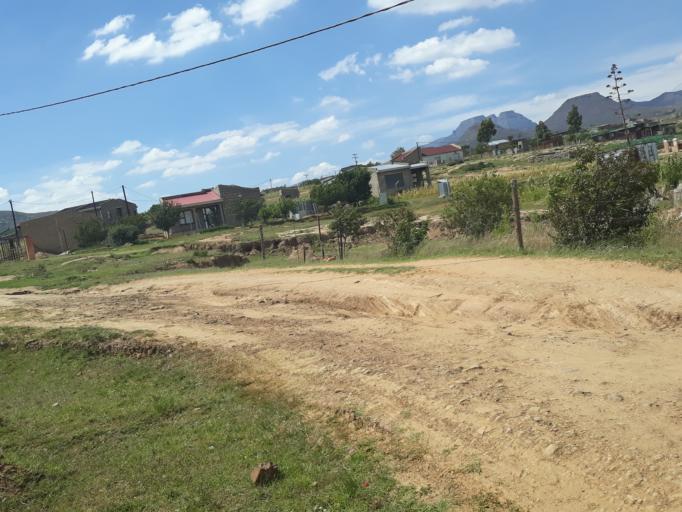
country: LS
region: Mohale's Hoek District
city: Mohale's Hoek
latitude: -30.1025
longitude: 27.4646
